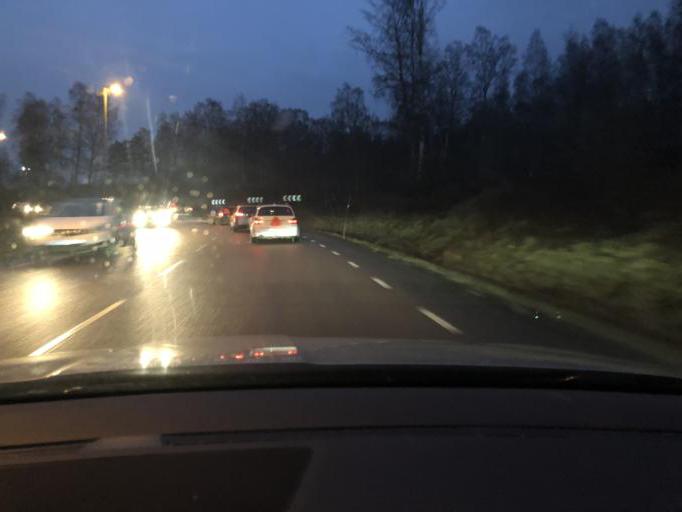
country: SE
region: Joenkoeping
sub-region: Jonkopings Kommun
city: Jonkoping
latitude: 57.7630
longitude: 14.1990
